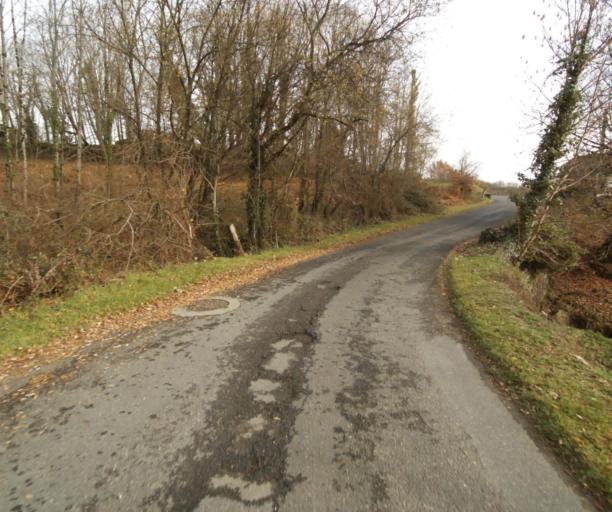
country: FR
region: Limousin
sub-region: Departement de la Correze
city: Saint-Mexant
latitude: 45.2633
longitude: 1.6750
